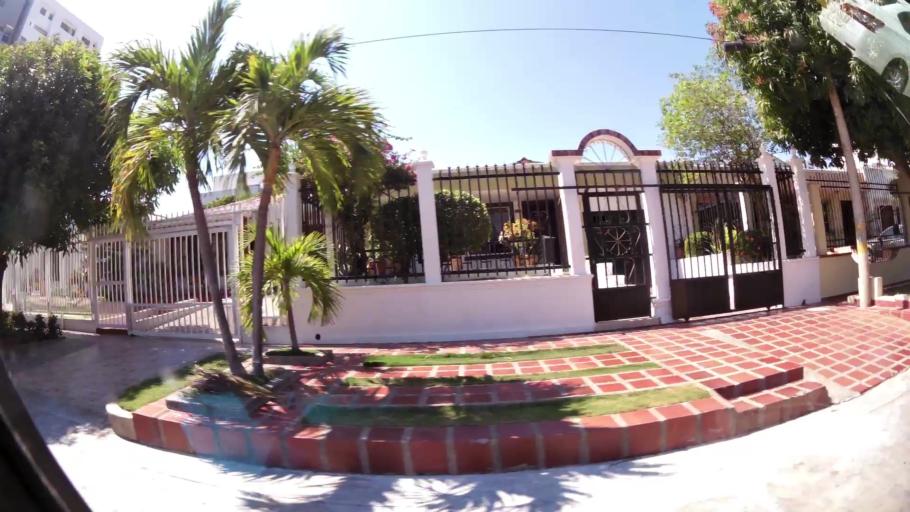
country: CO
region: Atlantico
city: Barranquilla
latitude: 11.0082
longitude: -74.7980
